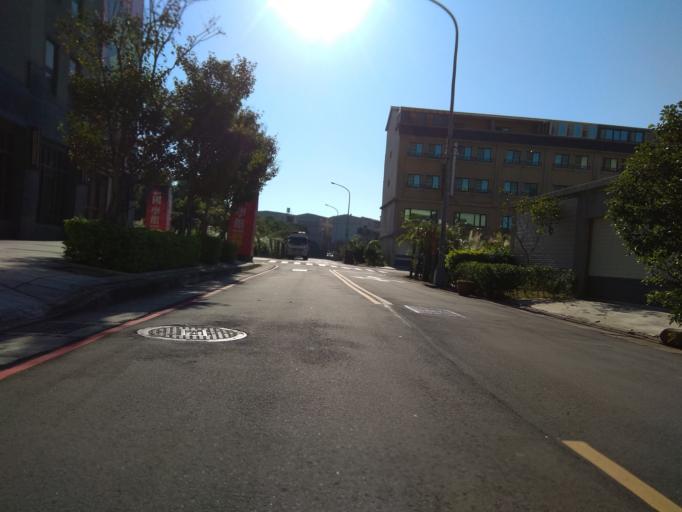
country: TW
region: Taiwan
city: Taoyuan City
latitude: 25.0199
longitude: 121.2190
